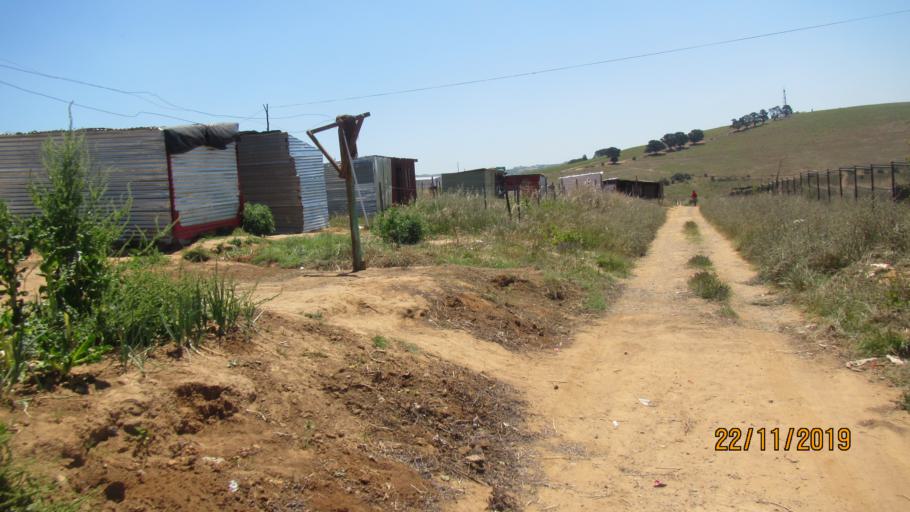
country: ZA
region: Western Cape
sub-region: Cape Winelands District Municipality
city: Stellenbosch
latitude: -33.9227
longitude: 18.8397
